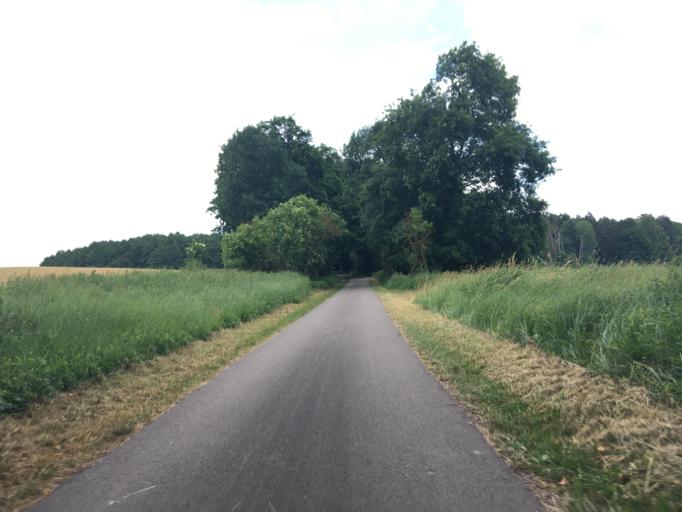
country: DE
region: Brandenburg
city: Althuttendorf
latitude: 53.0245
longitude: 13.8622
